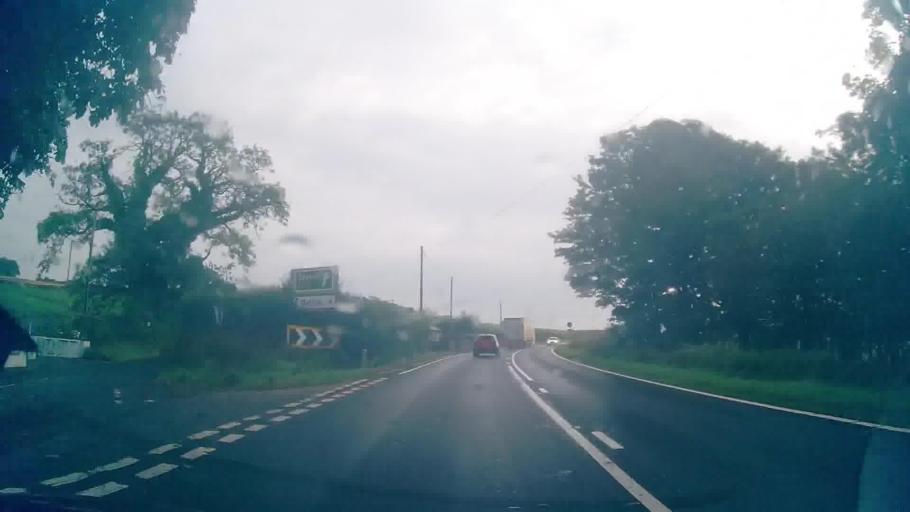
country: GB
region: Scotland
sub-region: Dumfries and Galloway
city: Lochmaben
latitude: 55.0593
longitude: -3.4767
